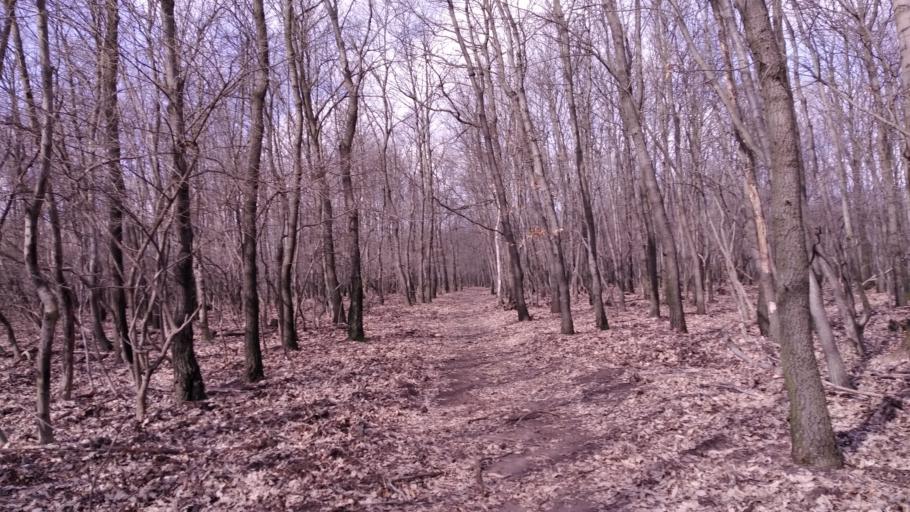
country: HU
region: Komarom-Esztergom
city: Oroszlany
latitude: 47.4018
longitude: 18.3403
